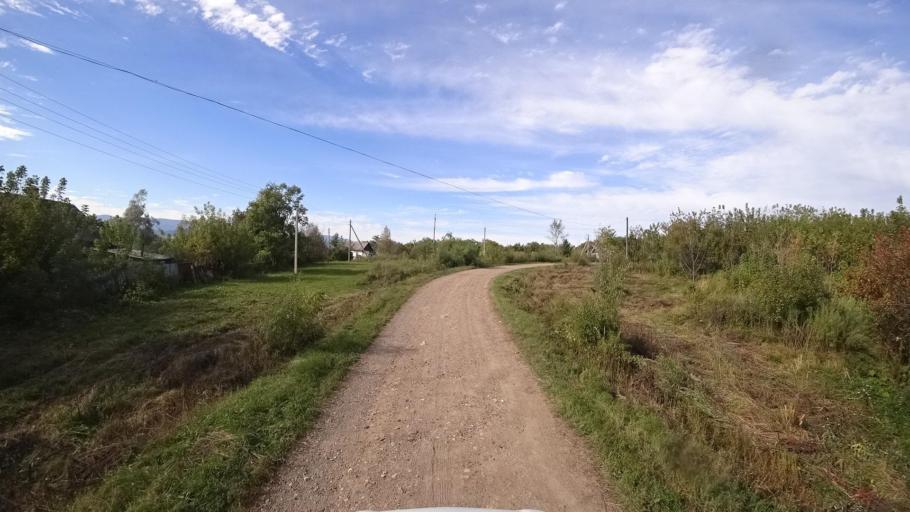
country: RU
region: Primorskiy
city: Dostoyevka
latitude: 44.2953
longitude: 133.4482
